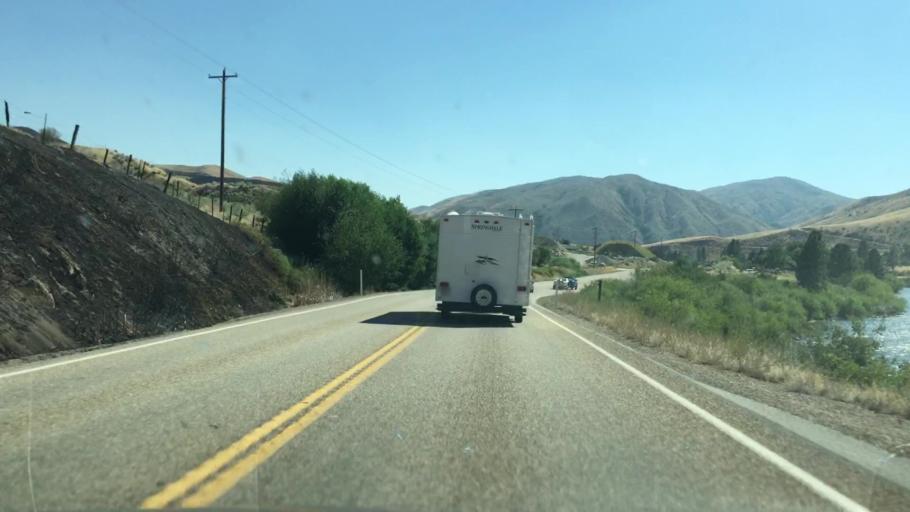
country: US
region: Idaho
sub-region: Gem County
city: Emmett
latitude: 44.0002
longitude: -116.1818
